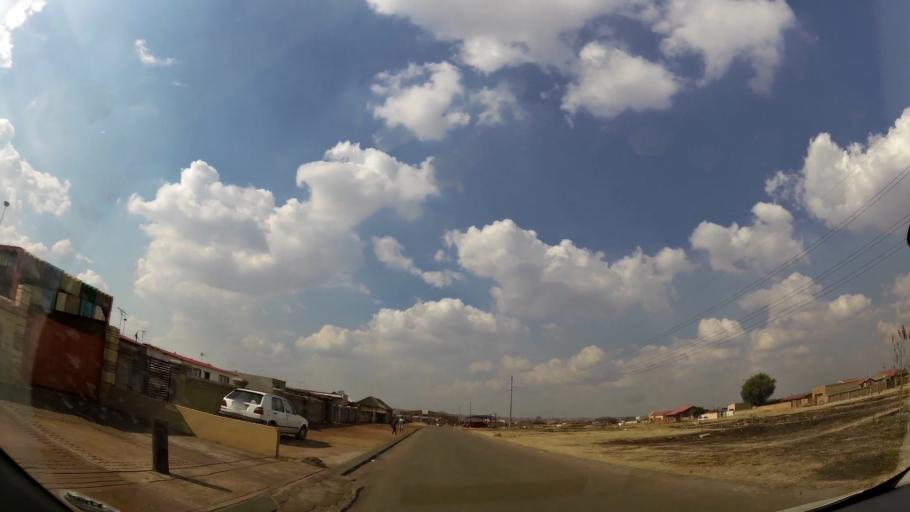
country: ZA
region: Gauteng
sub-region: Ekurhuleni Metropolitan Municipality
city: Germiston
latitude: -26.3588
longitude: 28.1633
